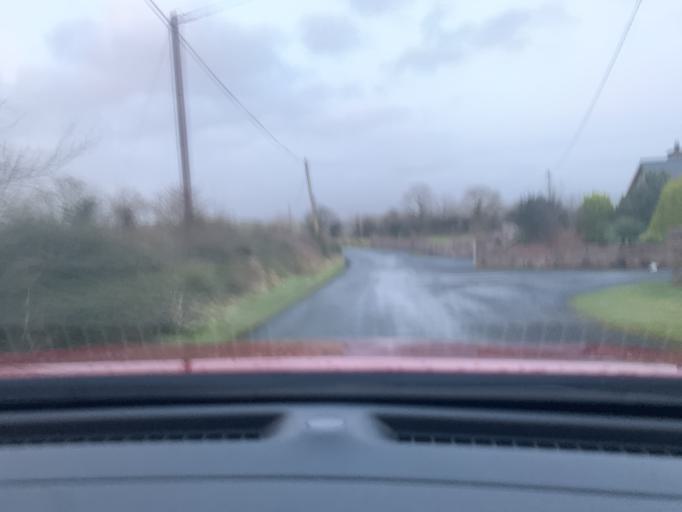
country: IE
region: Connaught
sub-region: Sligo
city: Ballymote
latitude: 54.0760
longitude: -8.3836
